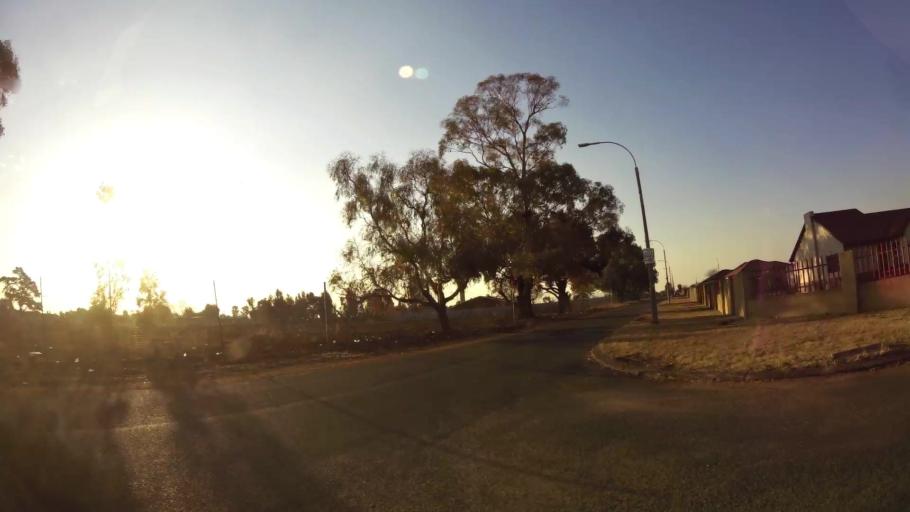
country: ZA
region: Gauteng
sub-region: West Rand District Municipality
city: Randfontein
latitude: -26.2057
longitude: 27.6481
